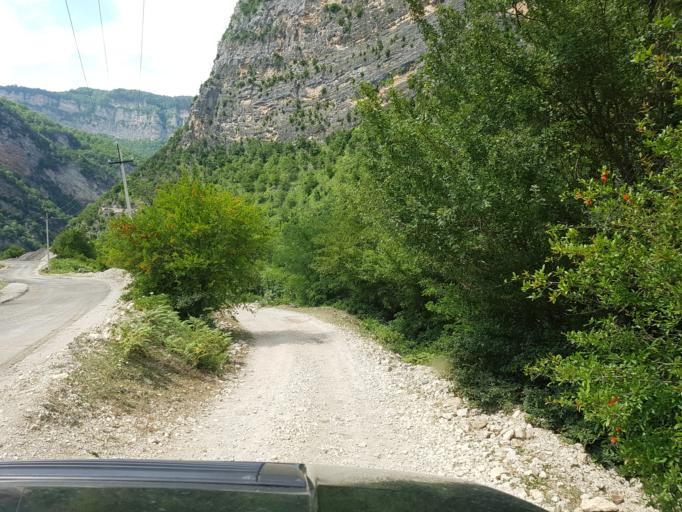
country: GE
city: Tqibuli
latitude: 42.5192
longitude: 42.8006
